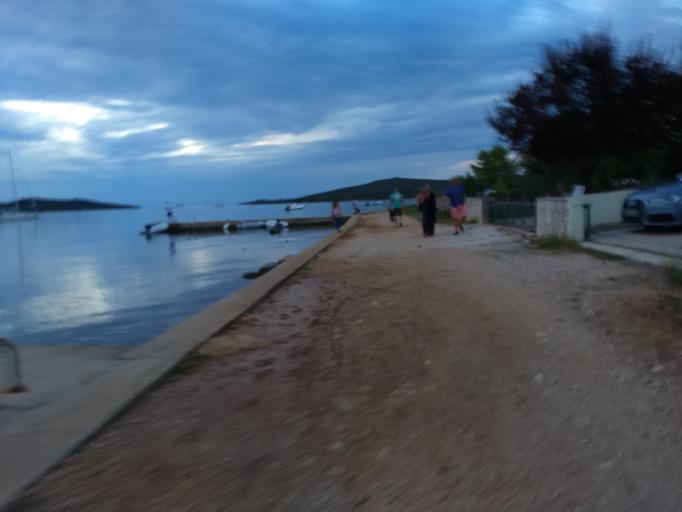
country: HR
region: Zadarska
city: Ugljan
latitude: 44.1355
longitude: 15.0704
